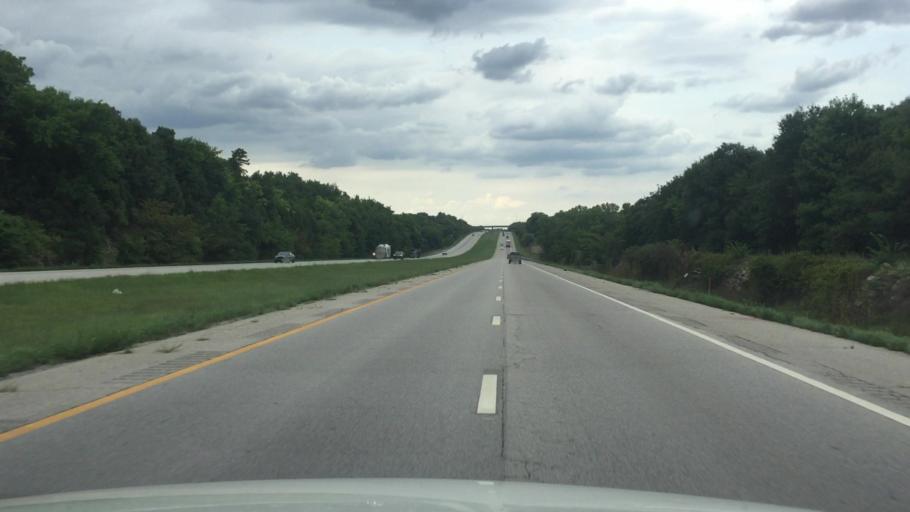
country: US
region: Missouri
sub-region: Cass County
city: Belton
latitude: 38.7880
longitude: -94.6769
